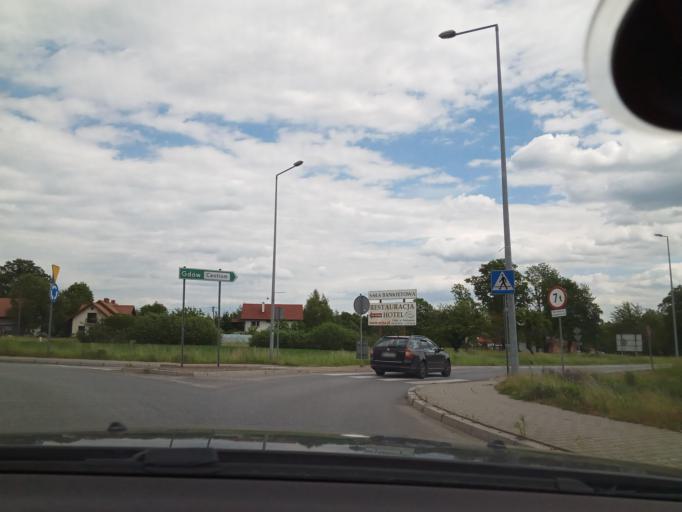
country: PL
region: Lesser Poland Voivodeship
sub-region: Powiat wielicki
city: Gdow
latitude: 49.9143
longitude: 20.1936
